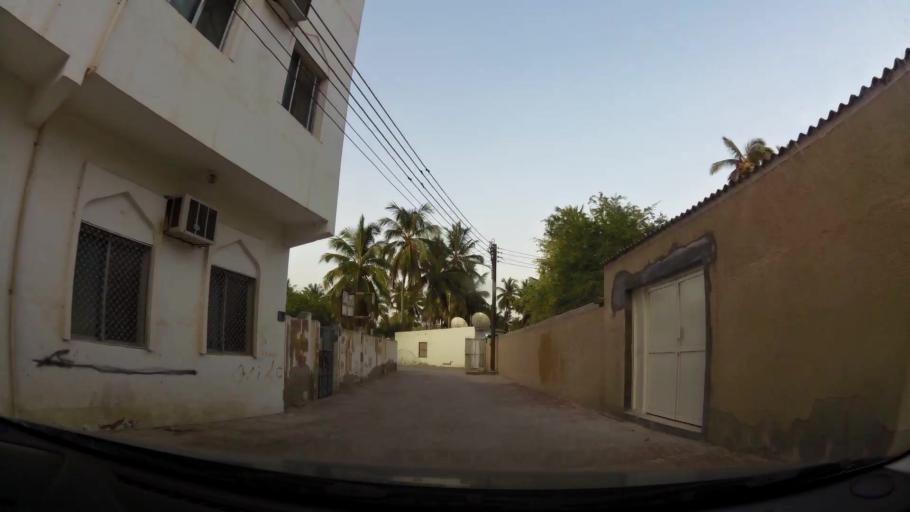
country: OM
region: Zufar
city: Salalah
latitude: 17.0178
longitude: 54.1172
